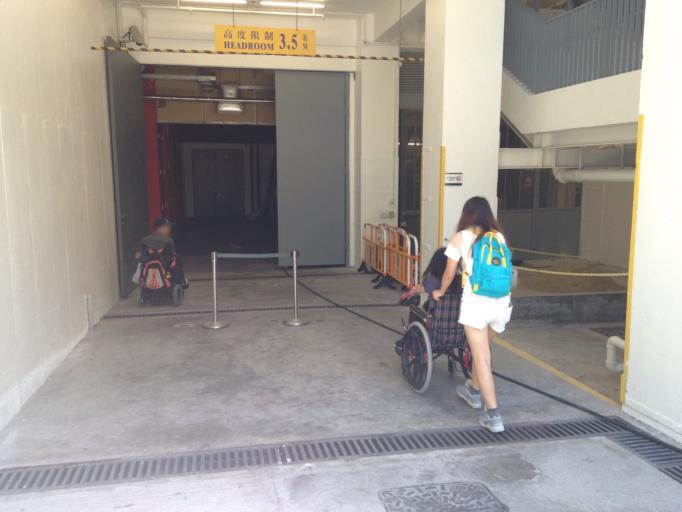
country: HK
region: Sham Shui Po
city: Sham Shui Po
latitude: 22.3350
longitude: 114.1655
